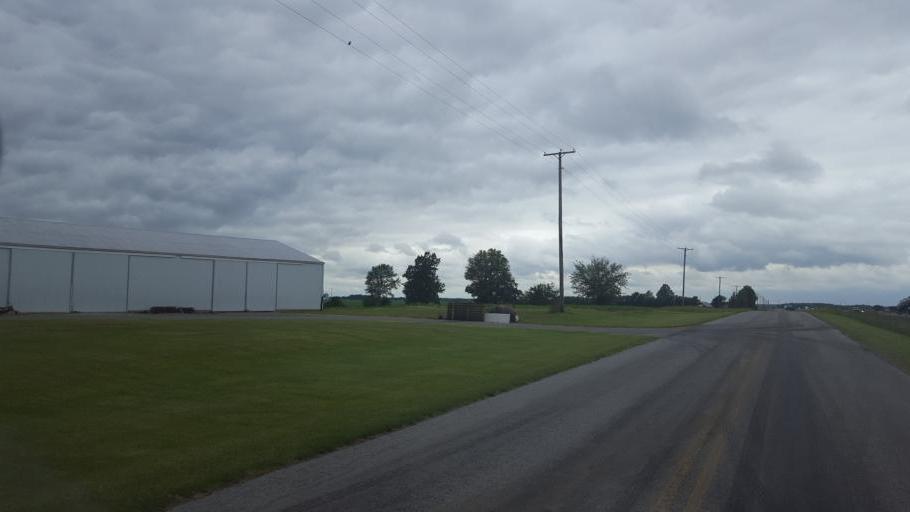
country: US
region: Ohio
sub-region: Marion County
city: Marion
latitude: 40.7089
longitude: -83.1693
